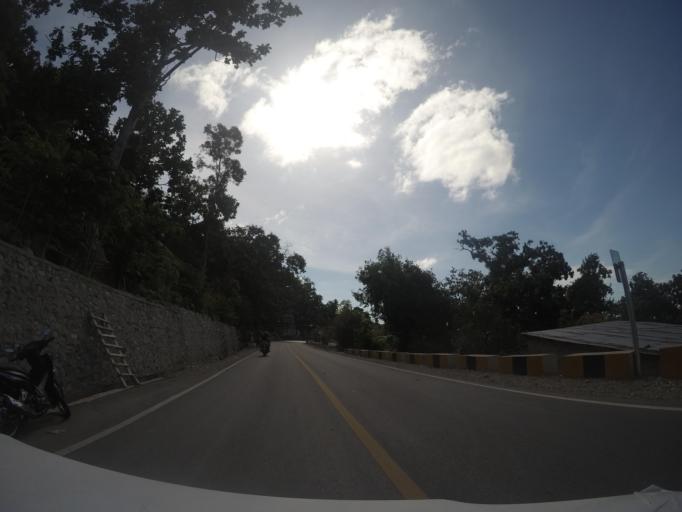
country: TL
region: Baucau
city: Baucau
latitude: -8.4598
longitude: 126.4595
